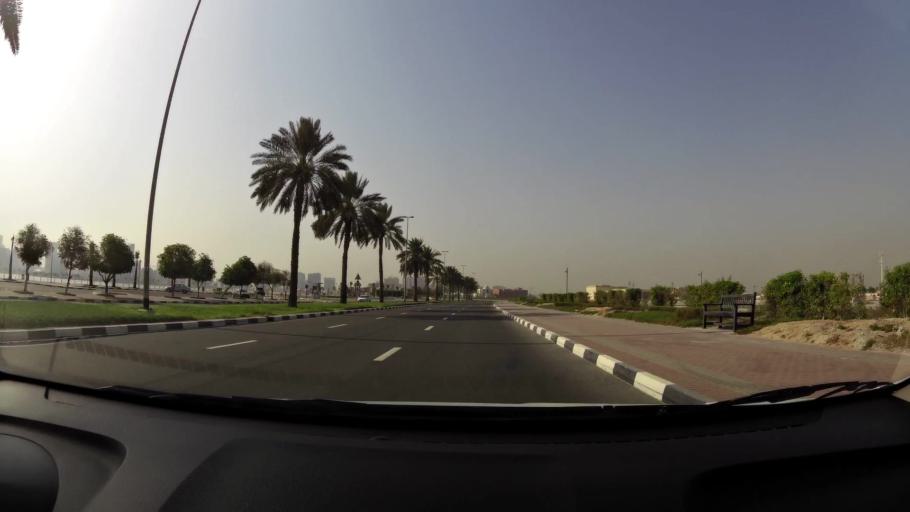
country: AE
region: Ash Shariqah
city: Sharjah
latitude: 25.3021
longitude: 55.3486
